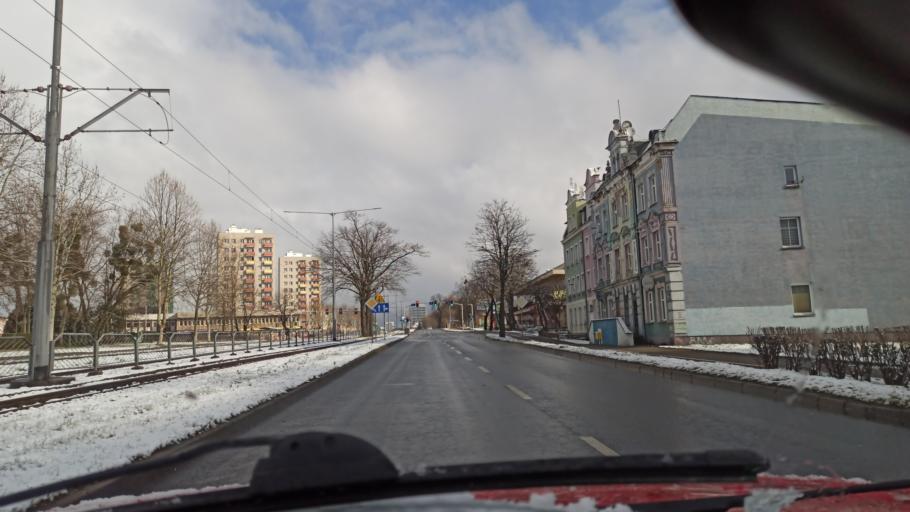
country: PL
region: Warmian-Masurian Voivodeship
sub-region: Powiat elblaski
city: Elblag
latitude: 54.1713
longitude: 19.4047
